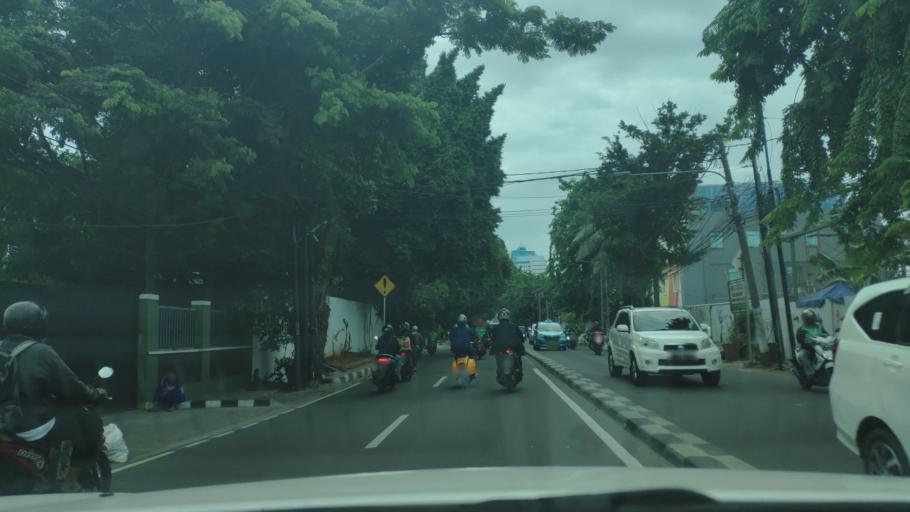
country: ID
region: Jakarta Raya
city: Jakarta
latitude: -6.1891
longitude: 106.8053
